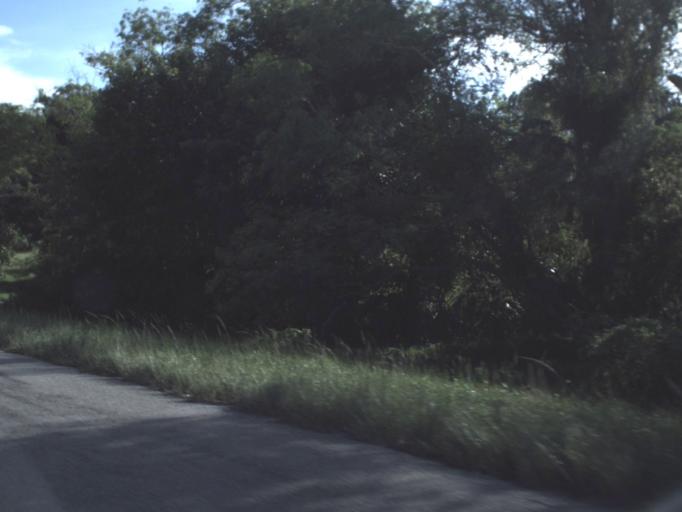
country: US
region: Florida
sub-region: Charlotte County
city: Punta Gorda
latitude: 26.9387
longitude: -82.0187
